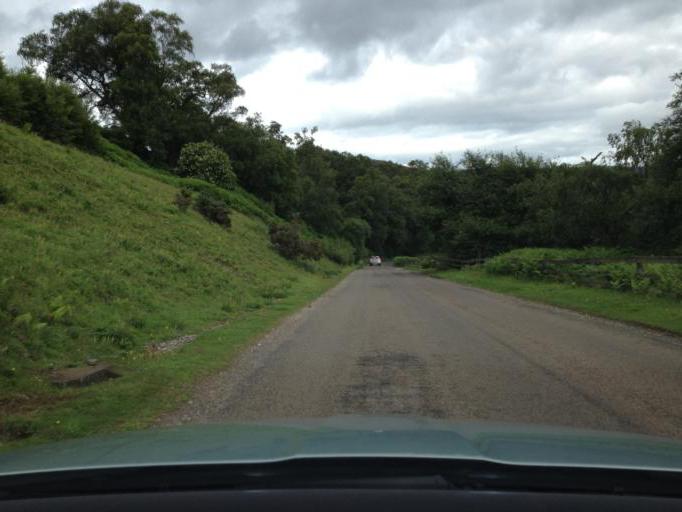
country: GB
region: Scotland
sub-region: Aberdeenshire
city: Aboyne
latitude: 56.8979
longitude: -2.7615
